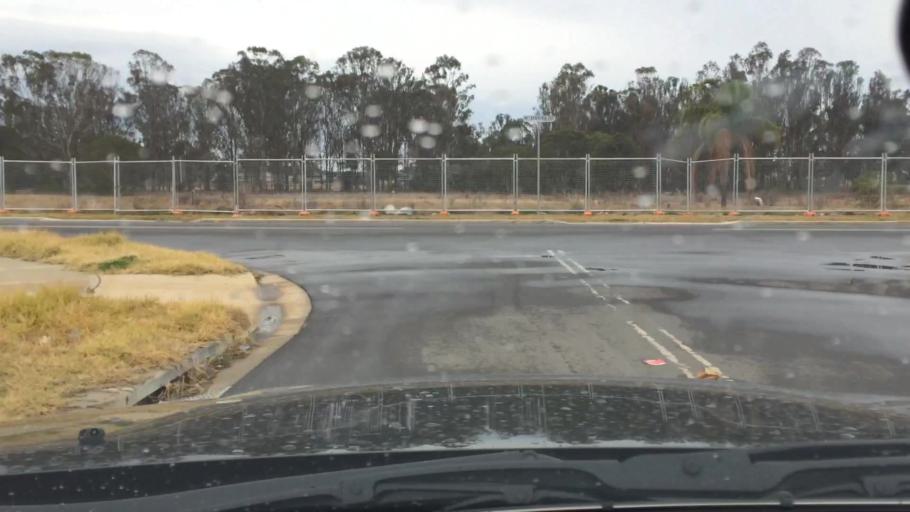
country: AU
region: New South Wales
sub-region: Campbelltown Municipality
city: Denham Court
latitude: -33.9617
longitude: 150.8471
